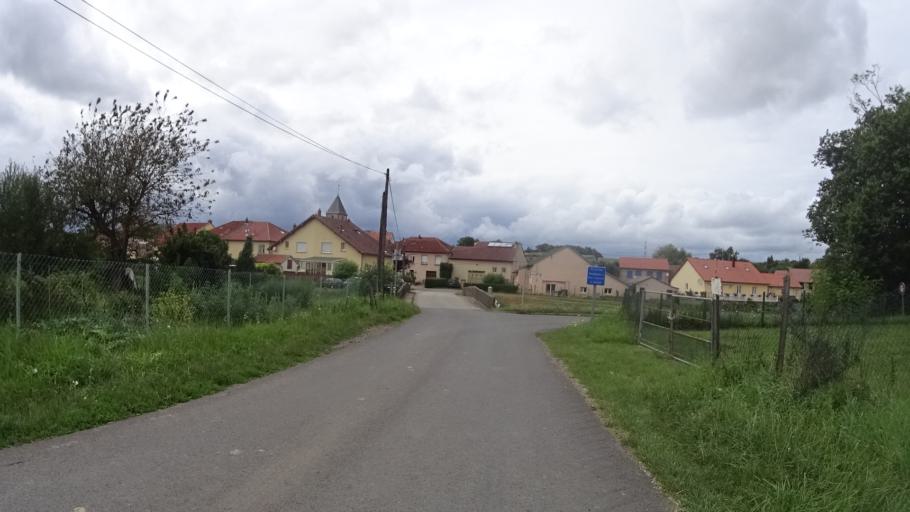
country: FR
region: Lorraine
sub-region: Departement de la Moselle
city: Sarrebourg
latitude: 48.6941
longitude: 7.0518
